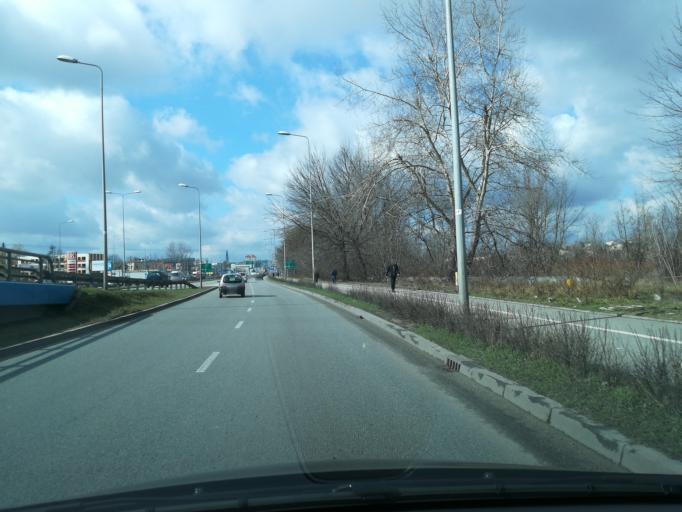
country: PL
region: Silesian Voivodeship
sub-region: Czestochowa
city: Czestochowa
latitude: 50.8184
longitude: 19.1355
